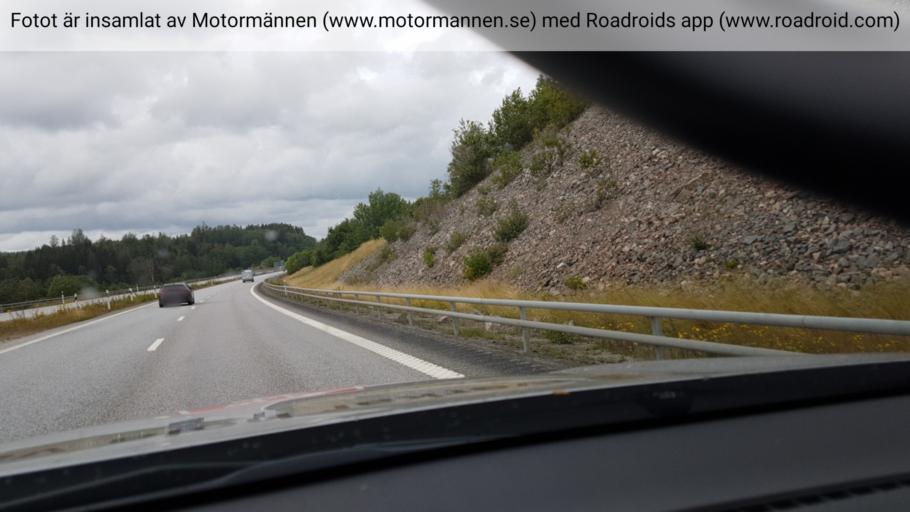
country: SE
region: Vaestra Goetaland
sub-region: Munkedals Kommun
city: Munkedal
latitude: 58.4929
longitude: 11.5753
